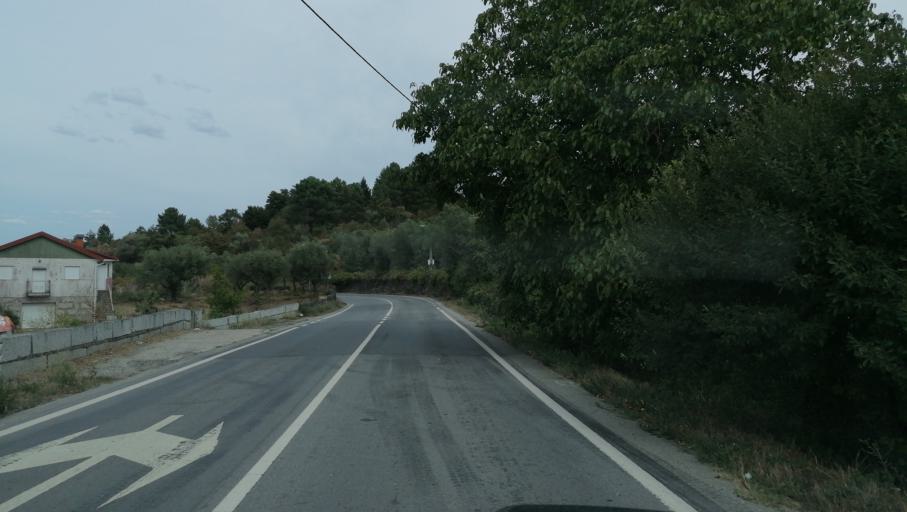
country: PT
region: Vila Real
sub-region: Vila Pouca de Aguiar
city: Vila Pouca de Aguiar
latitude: 41.5303
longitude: -7.6117
